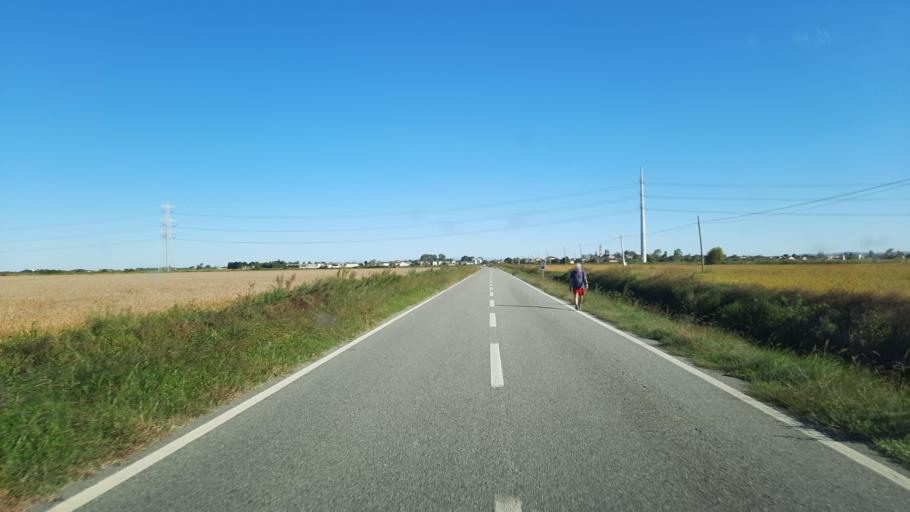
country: IT
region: Piedmont
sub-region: Provincia di Vercelli
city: Lignana
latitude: 45.2799
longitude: 8.3471
